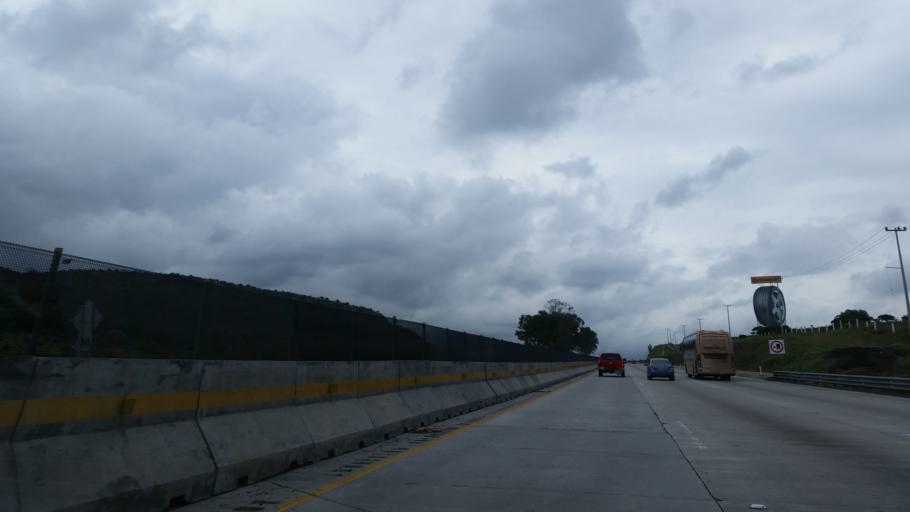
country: MX
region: Hidalgo
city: Tepeji de Ocampo
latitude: 19.9144
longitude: -99.3620
